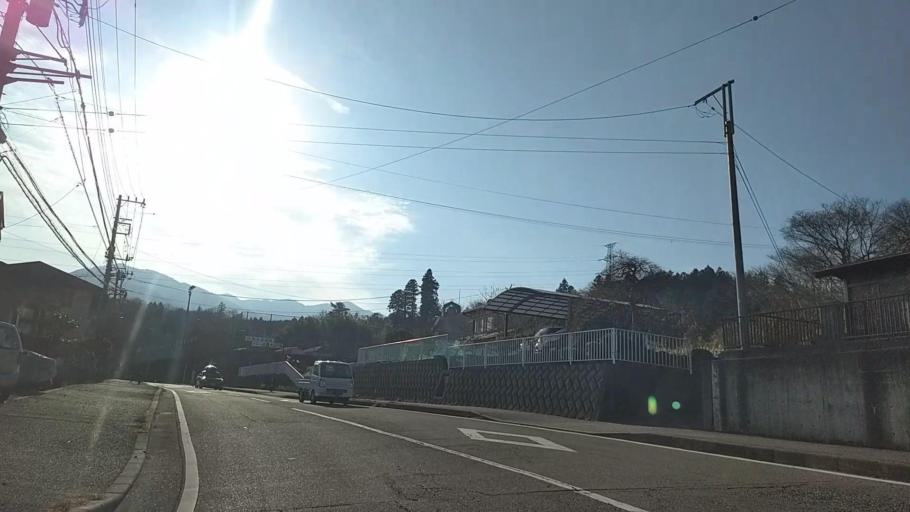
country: JP
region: Yamanashi
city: Uenohara
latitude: 35.5464
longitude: 139.2189
